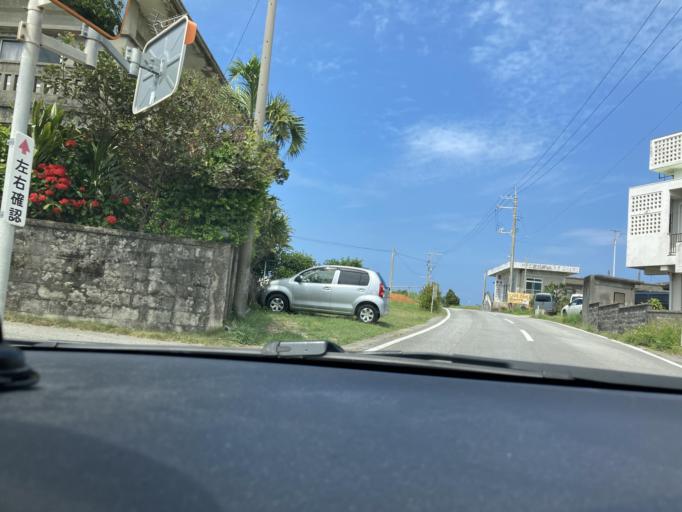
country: JP
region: Okinawa
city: Ishikawa
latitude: 26.4399
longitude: 127.7710
